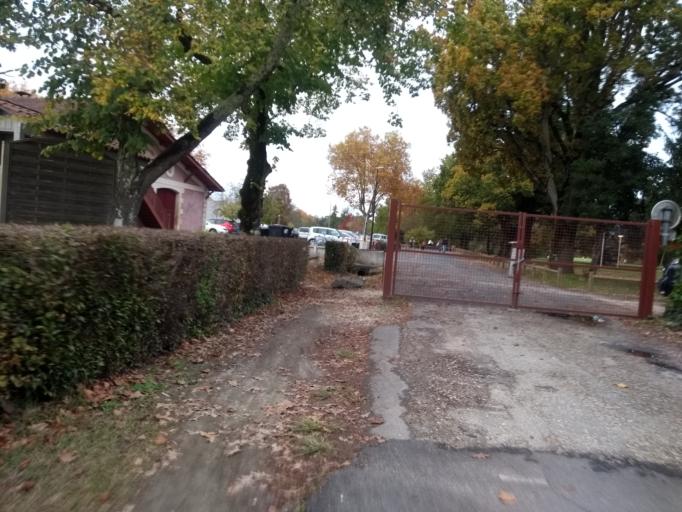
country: FR
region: Aquitaine
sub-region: Departement de la Gironde
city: Gradignan
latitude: 44.7665
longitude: -0.6078
